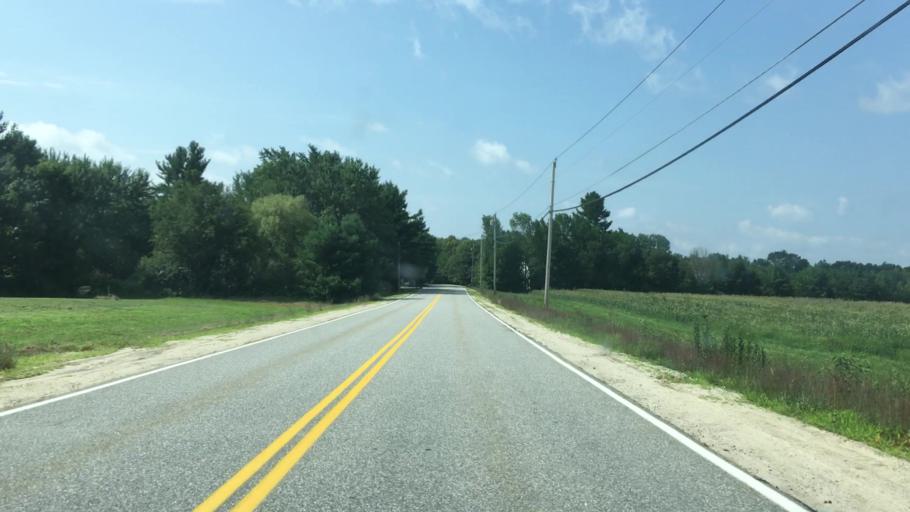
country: US
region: Maine
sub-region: Cumberland County
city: Raymond
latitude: 43.9479
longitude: -70.4373
